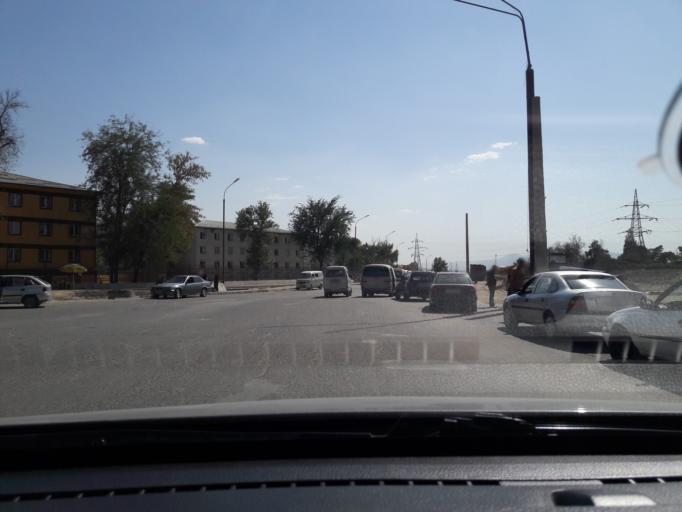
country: TJ
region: Dushanbe
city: Dushanbe
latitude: 38.5321
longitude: 68.7364
